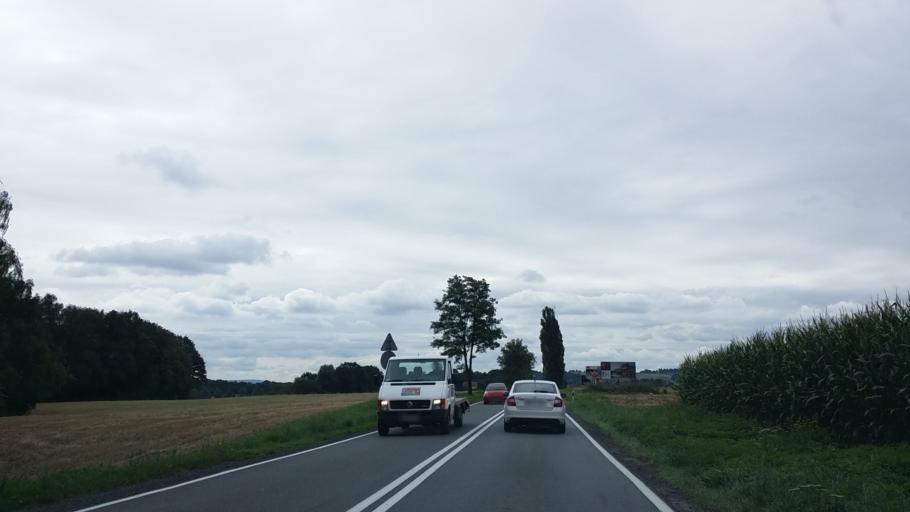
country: PL
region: Lesser Poland Voivodeship
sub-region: Powiat oswiecimski
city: Zator
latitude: 49.9561
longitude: 19.4433
